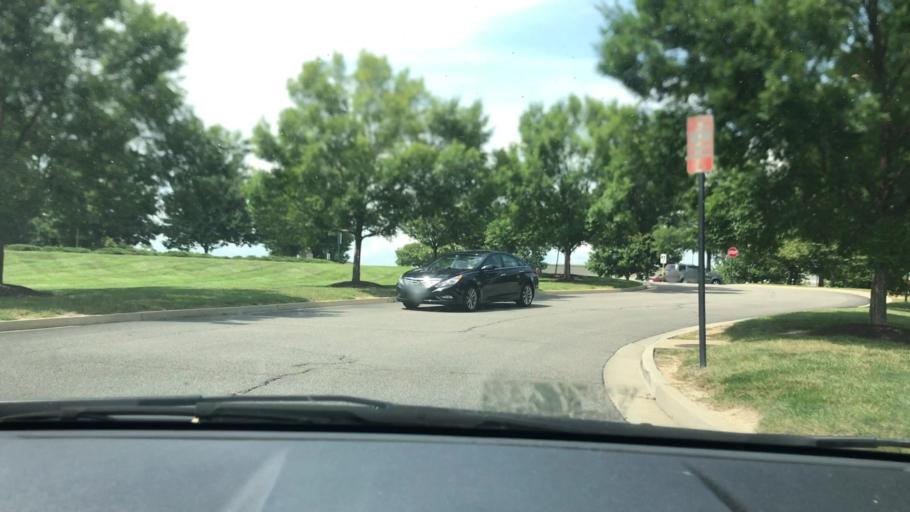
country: US
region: Virginia
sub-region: Henrico County
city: Wyndham
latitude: 37.6800
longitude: -77.5895
